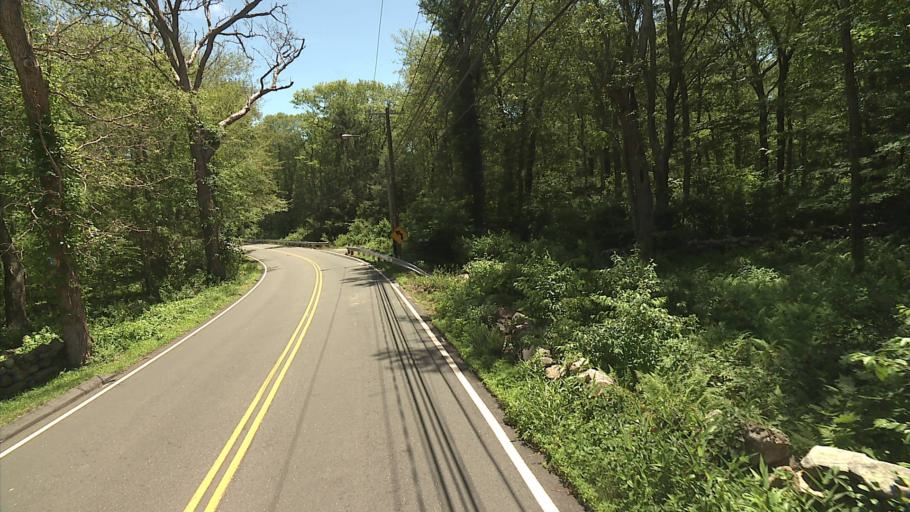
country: US
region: Connecticut
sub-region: New London County
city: Old Mystic
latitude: 41.3721
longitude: -71.9085
